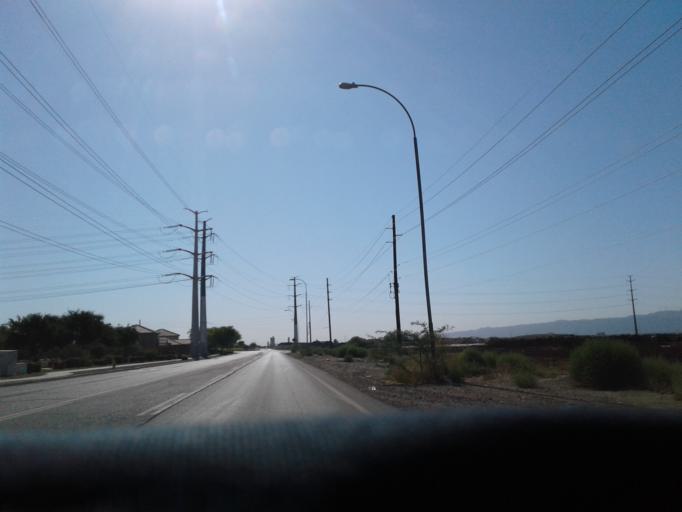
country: US
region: Arizona
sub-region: Maricopa County
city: Laveen
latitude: 33.4081
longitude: -112.1898
